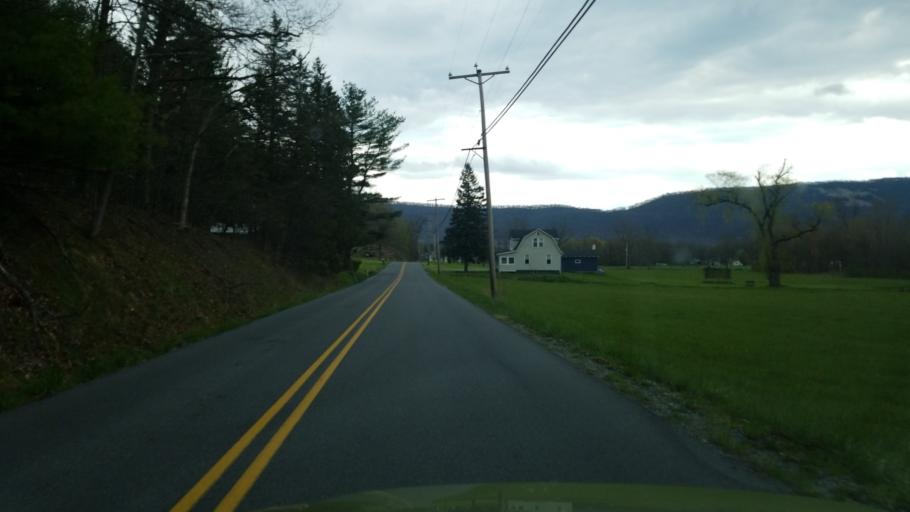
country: US
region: Pennsylvania
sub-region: Blair County
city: Tipton
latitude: 40.6434
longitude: -78.3096
